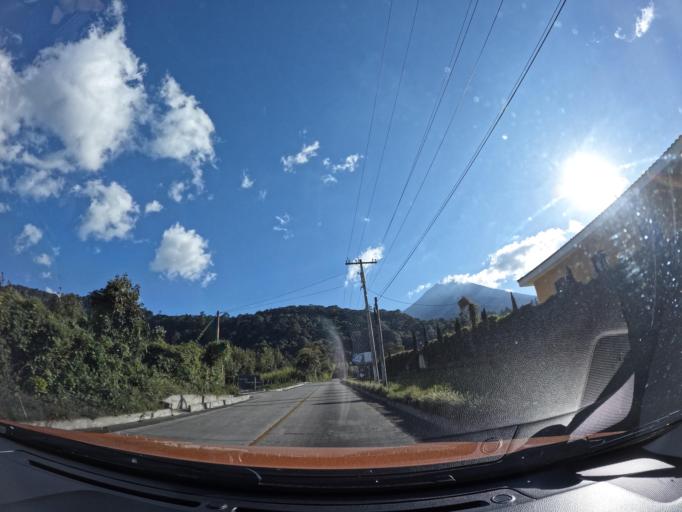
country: GT
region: Sacatepequez
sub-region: Municipio de Santa Maria de Jesus
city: Santa Maria de Jesus
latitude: 14.5160
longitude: -90.7222
